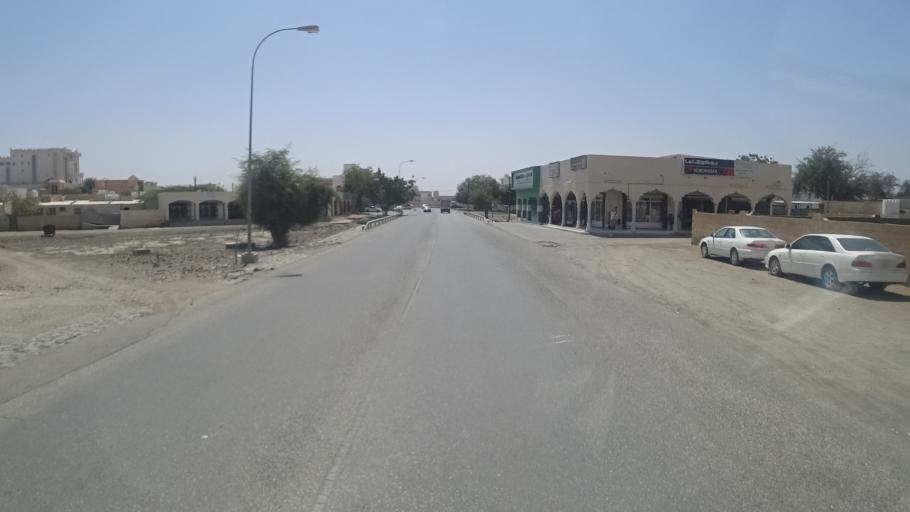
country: OM
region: Ash Sharqiyah
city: Ibra'
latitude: 22.6898
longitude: 58.5432
